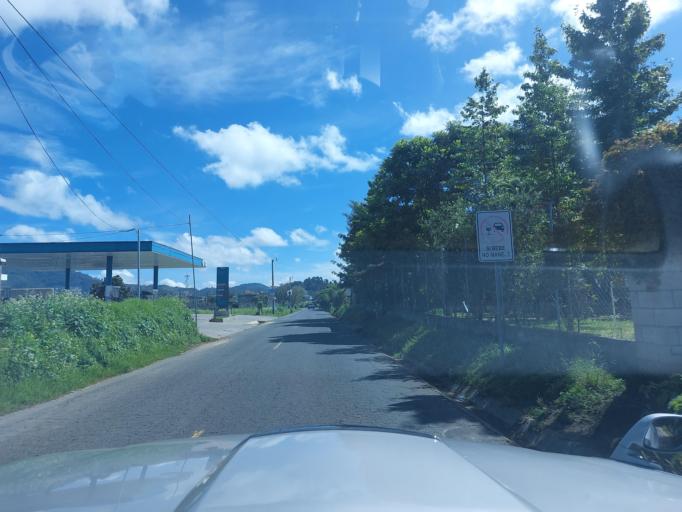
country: GT
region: Chimaltenango
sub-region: Municipio de San Juan Comalapa
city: Comalapa
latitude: 14.7247
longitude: -90.8881
